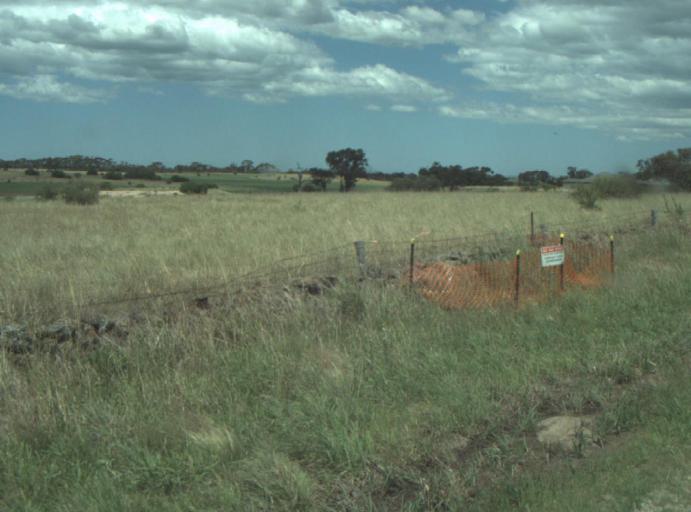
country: AU
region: Victoria
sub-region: Wyndham
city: Little River
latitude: -37.9164
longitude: 144.4629
